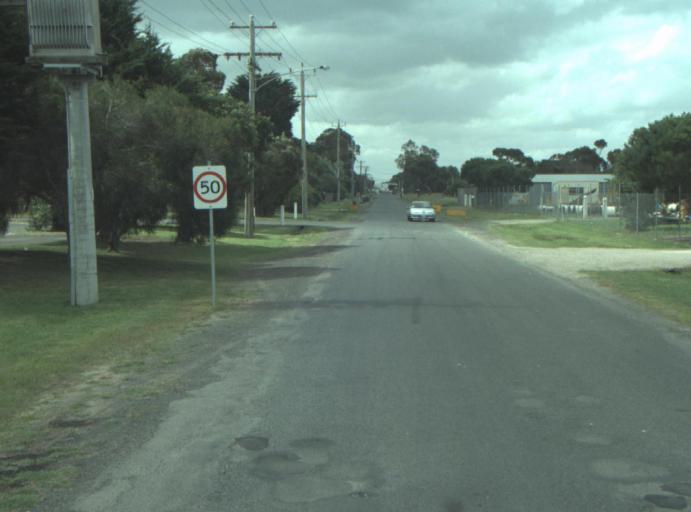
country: AU
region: Victoria
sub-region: Greater Geelong
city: East Geelong
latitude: -38.1744
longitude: 144.4070
